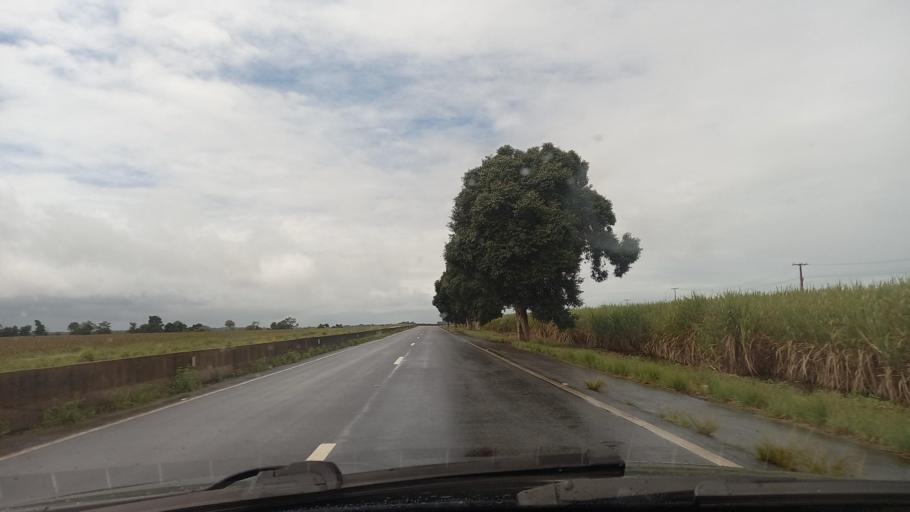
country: BR
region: Alagoas
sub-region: Campo Alegre
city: Campo Alegre
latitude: -9.8009
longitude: -36.2830
